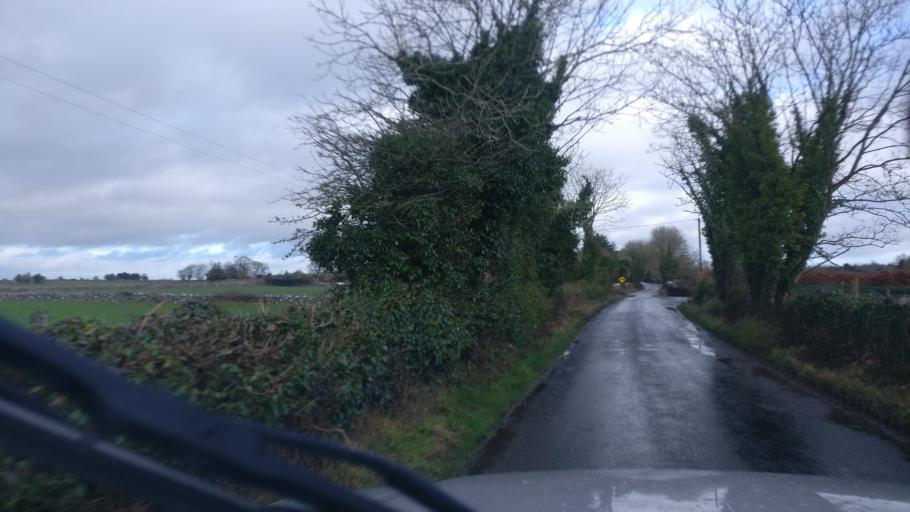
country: IE
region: Connaught
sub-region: County Galway
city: Athenry
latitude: 53.2451
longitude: -8.6577
